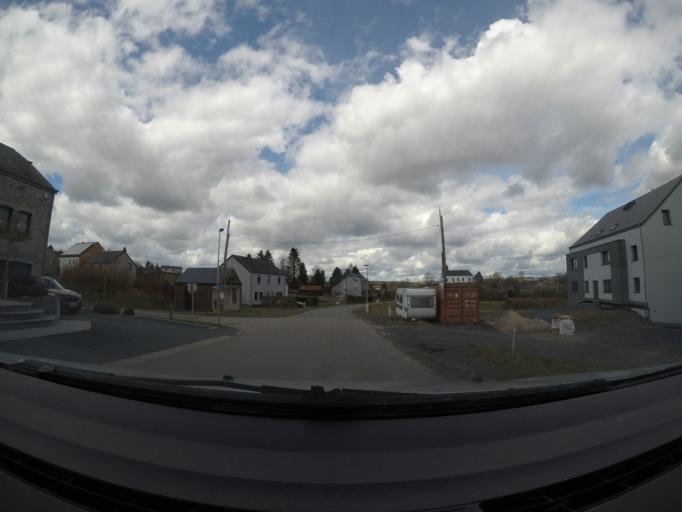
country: BE
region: Wallonia
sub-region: Province du Luxembourg
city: Leglise
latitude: 49.7979
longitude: 5.5402
